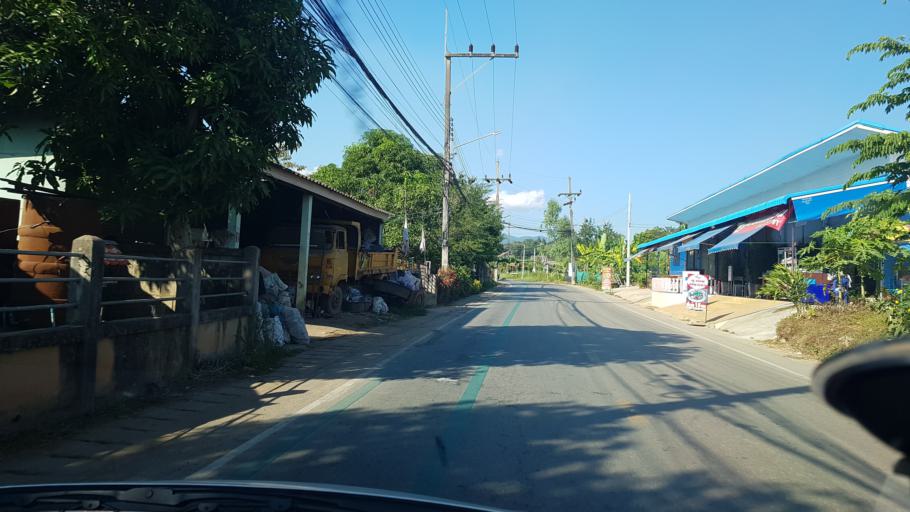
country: TH
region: Chiang Rai
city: Chiang Rai
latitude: 19.9458
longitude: 99.8105
